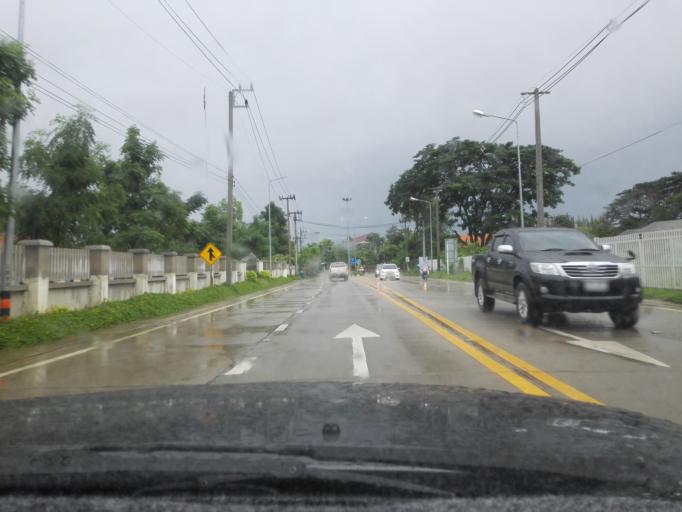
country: TH
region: Tak
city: Mae Sot
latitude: 16.7123
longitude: 98.5763
